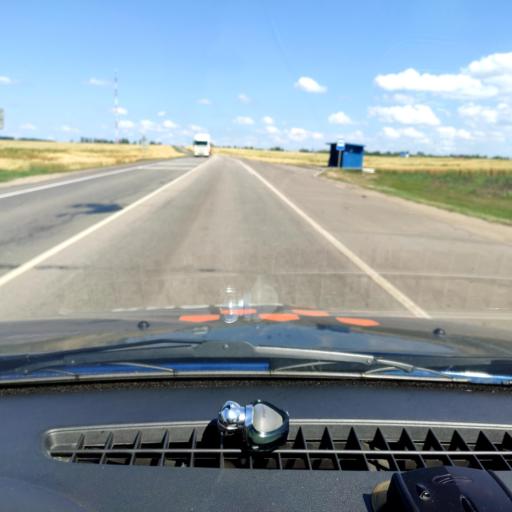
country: RU
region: Orjol
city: Livny
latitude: 52.4478
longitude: 37.4743
